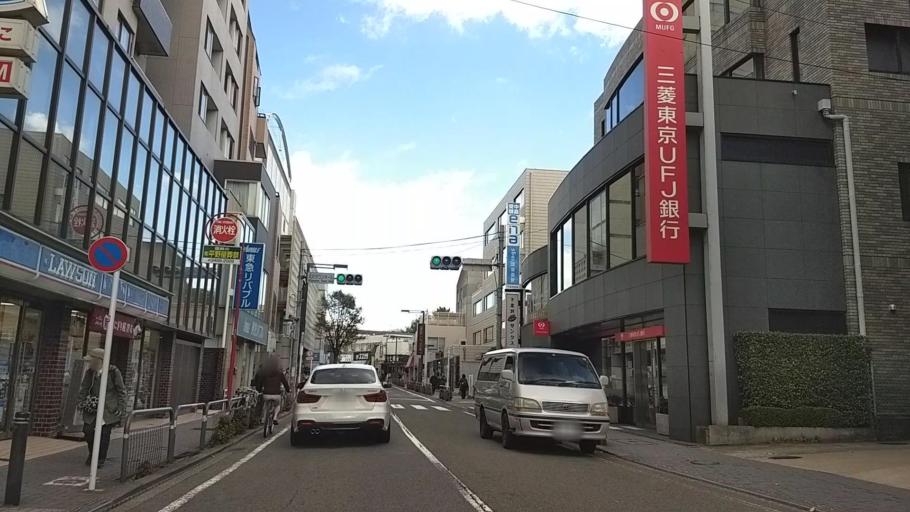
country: JP
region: Tokyo
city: Tokyo
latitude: 35.6615
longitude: 139.6696
